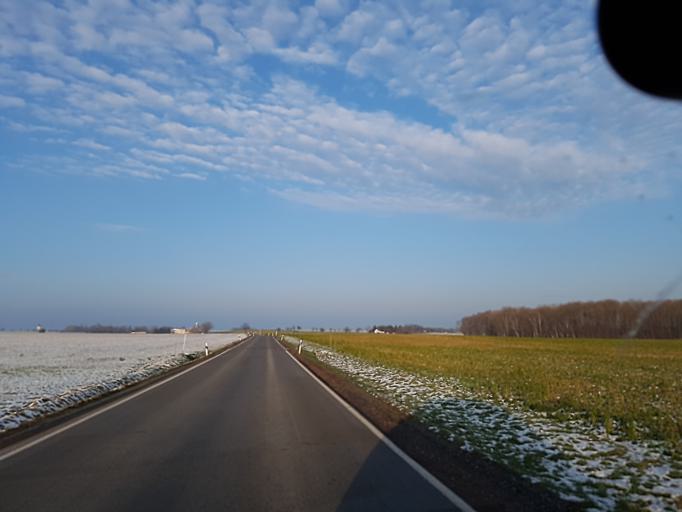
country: DE
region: Saxony
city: Naundorf
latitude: 51.2625
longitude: 13.1090
